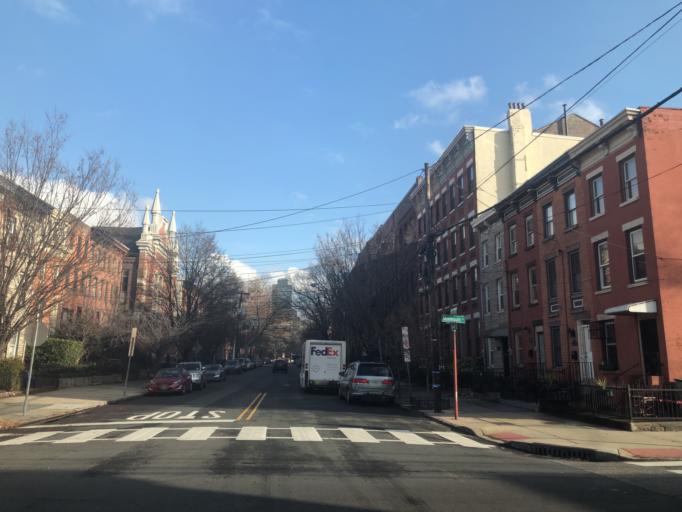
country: US
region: New Jersey
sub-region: Hudson County
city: Hoboken
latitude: 40.7279
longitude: -74.0485
